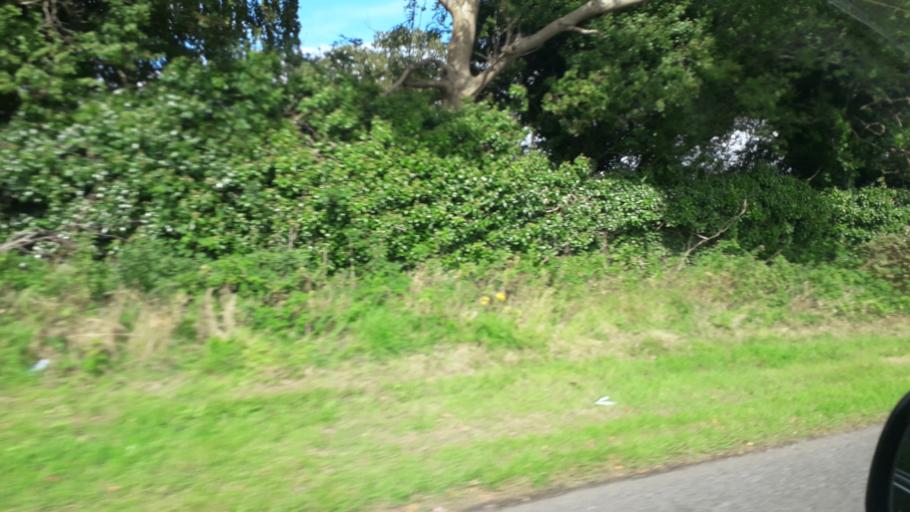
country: IE
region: Leinster
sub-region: Lu
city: Dundalk
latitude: 54.0338
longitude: -6.3687
